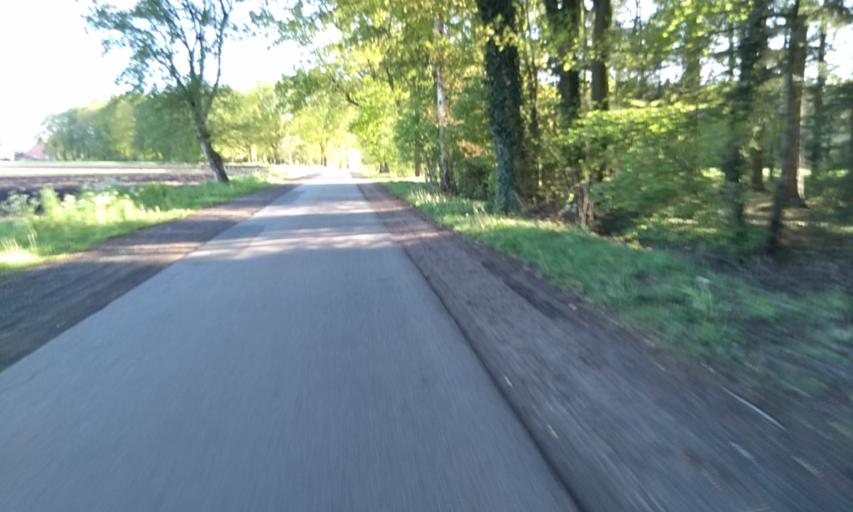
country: DE
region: Lower Saxony
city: Harsefeld
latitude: 53.4212
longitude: 9.5520
